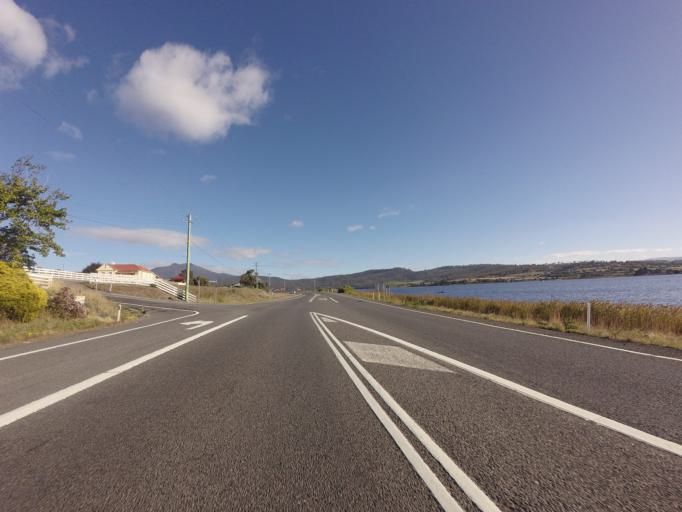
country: AU
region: Tasmania
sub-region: Glenorchy
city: Granton
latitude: -42.7479
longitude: 147.2198
